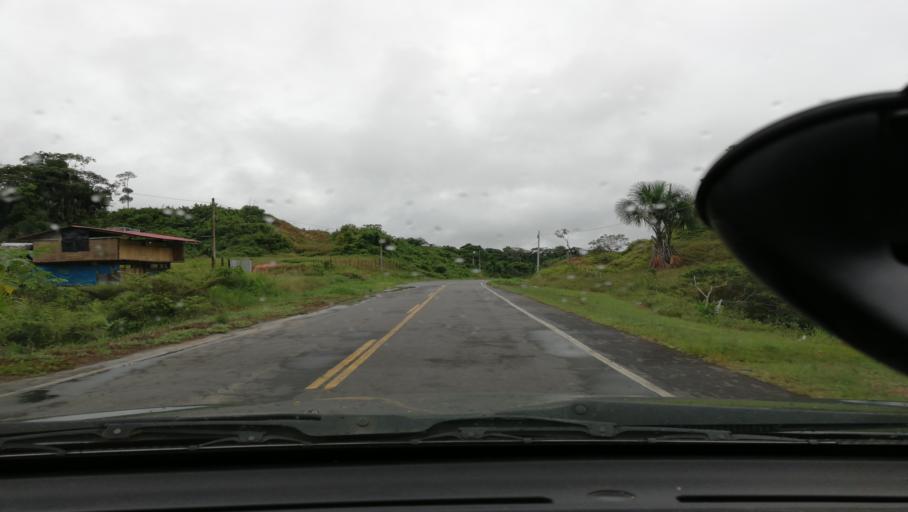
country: PE
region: Loreto
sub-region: Provincia de Loreto
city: Nauta
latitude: -4.3653
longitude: -73.5588
